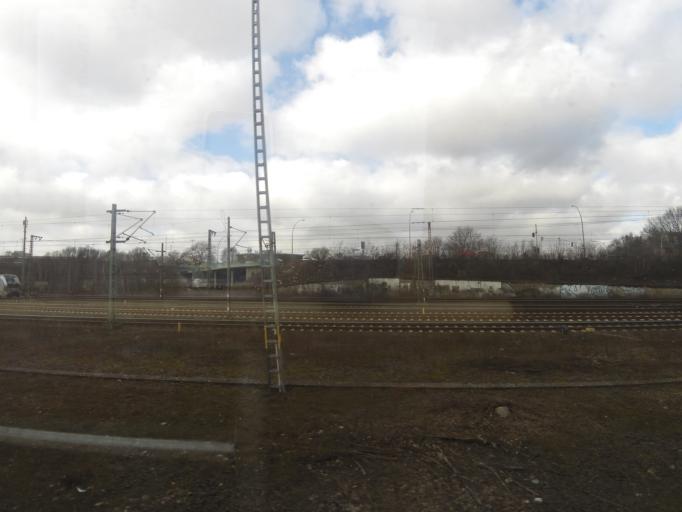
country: DE
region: Hamburg
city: Harburg
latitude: 53.4587
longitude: 9.9915
